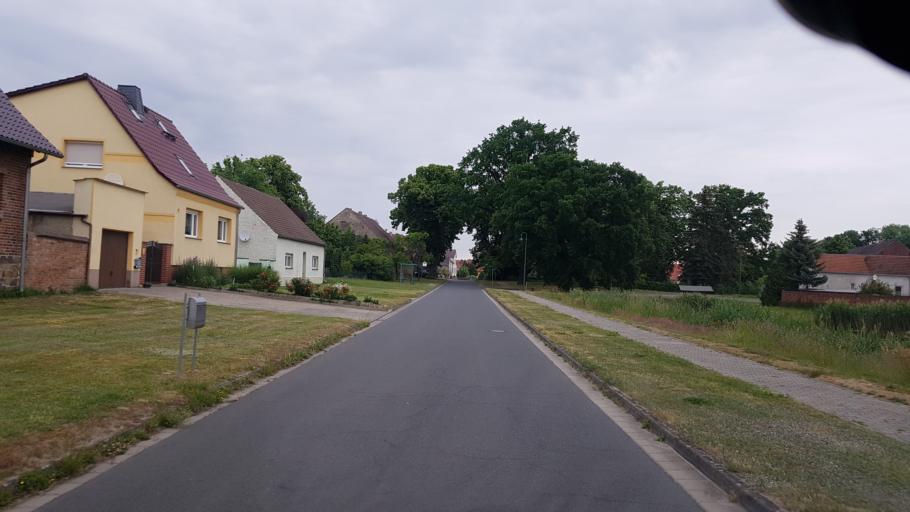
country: DE
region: Brandenburg
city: Herzberg
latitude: 51.7843
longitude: 13.2748
